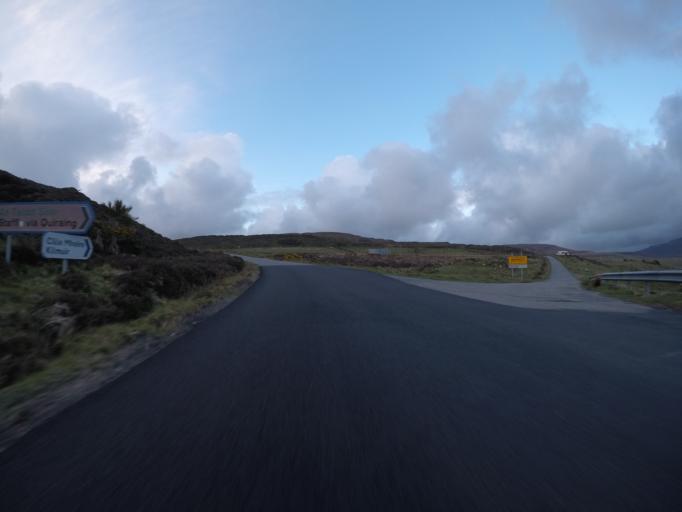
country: GB
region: Scotland
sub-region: Highland
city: Portree
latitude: 57.5932
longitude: -6.3736
